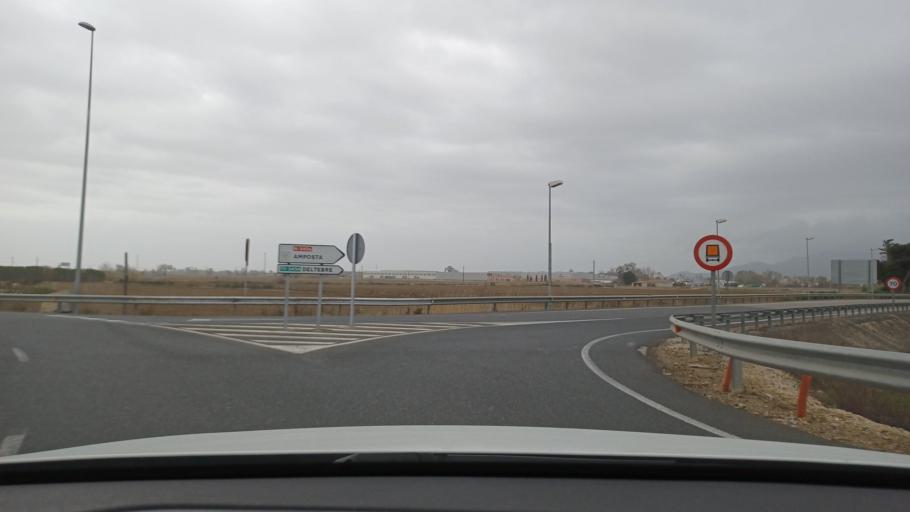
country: ES
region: Catalonia
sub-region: Provincia de Tarragona
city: Amposta
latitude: 40.7218
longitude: 0.5885
